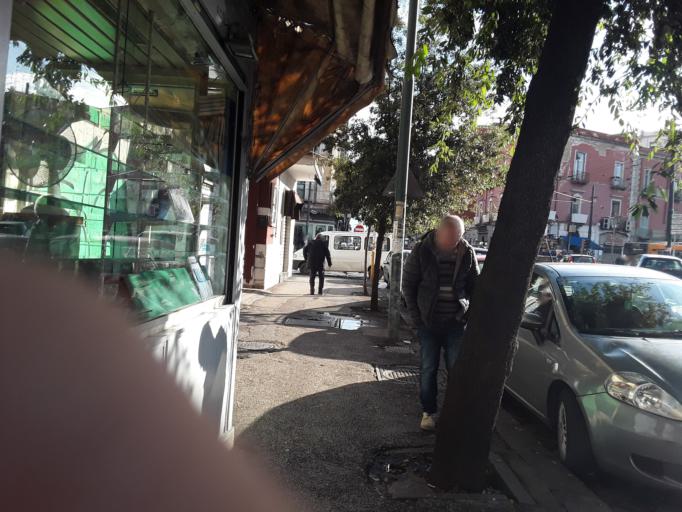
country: IT
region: Campania
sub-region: Provincia di Napoli
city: Napoli
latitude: 40.8557
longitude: 14.2676
